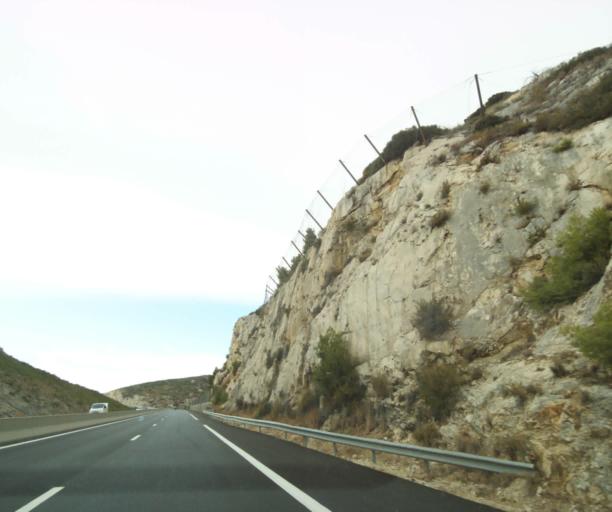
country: FR
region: Provence-Alpes-Cote d'Azur
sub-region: Departement des Bouches-du-Rhone
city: Carry-le-Rouet
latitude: 43.3403
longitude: 5.1531
